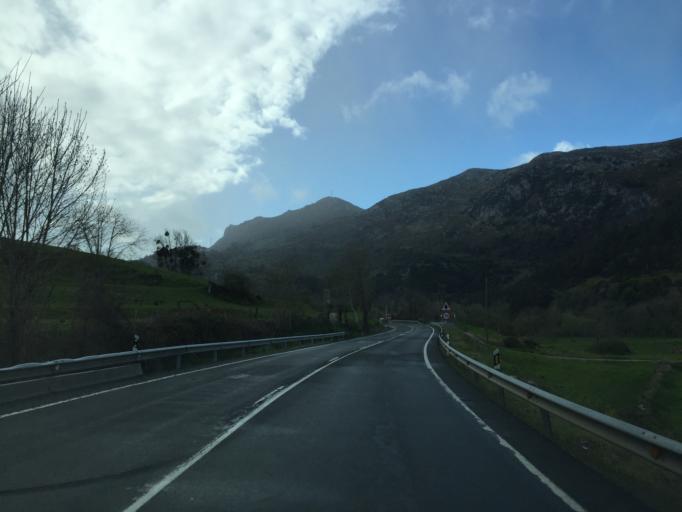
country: ES
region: Cantabria
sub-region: Provincia de Cantabria
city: Tresviso
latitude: 43.3267
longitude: -4.5716
